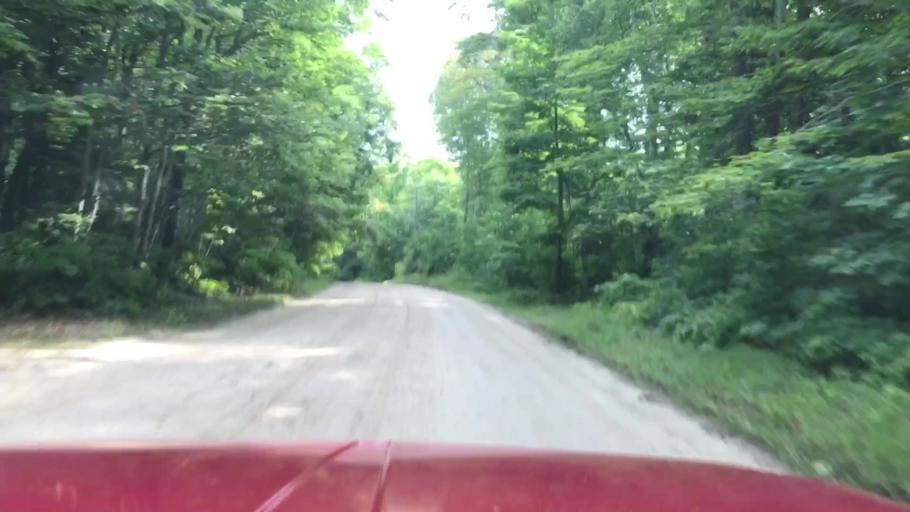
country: US
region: Michigan
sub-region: Charlevoix County
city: Charlevoix
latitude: 45.7455
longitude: -85.5518
